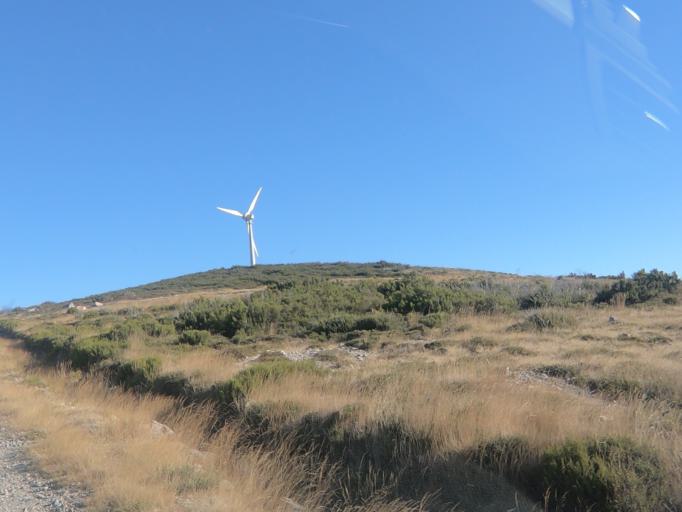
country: PT
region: Vila Real
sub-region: Vila Real
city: Vila Real
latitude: 41.3566
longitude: -7.7737
